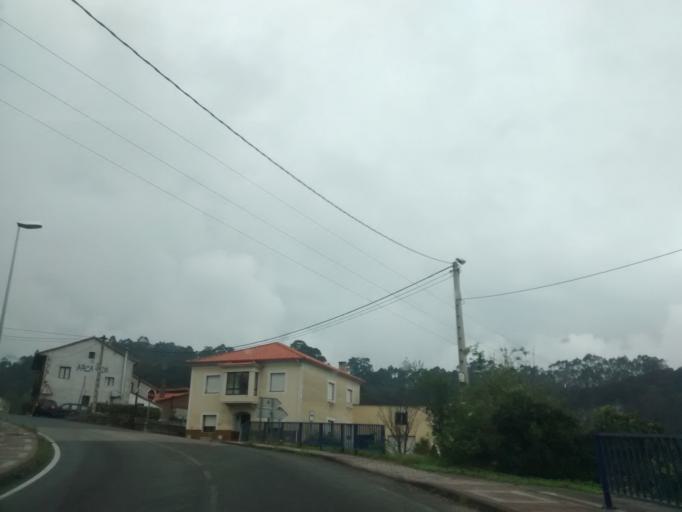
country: ES
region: Cantabria
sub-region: Provincia de Cantabria
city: Camargo
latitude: 43.4023
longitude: -3.8859
